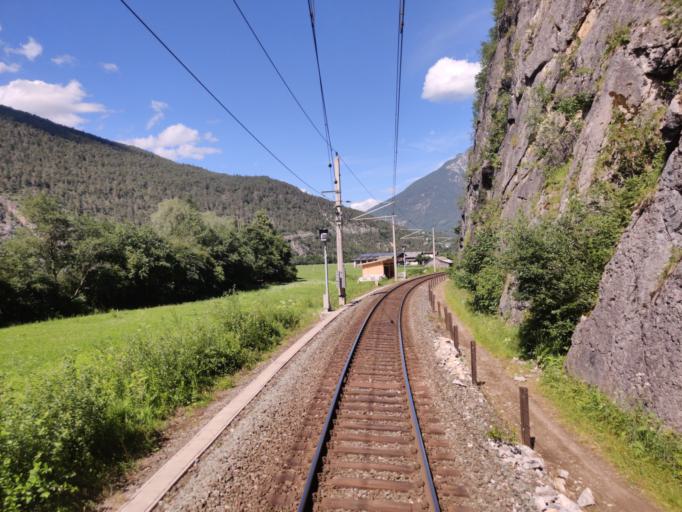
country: AT
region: Tyrol
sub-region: Politischer Bezirk Imst
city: Imsterberg
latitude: 47.2101
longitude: 10.7000
